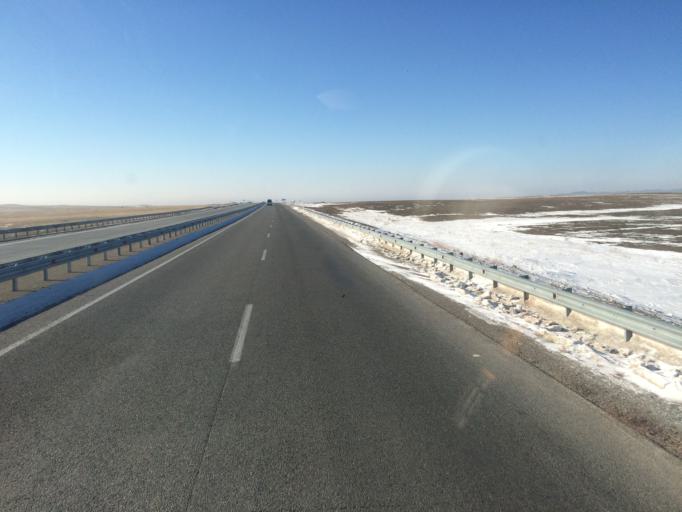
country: KZ
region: Zhambyl
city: Georgiyevka
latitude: 43.3595
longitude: 74.6245
